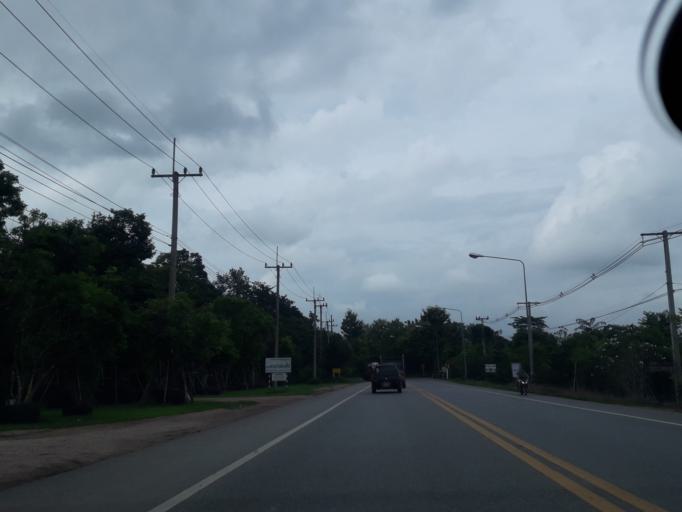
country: TH
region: Sara Buri
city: Wihan Daeng
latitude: 14.4123
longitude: 101.1008
